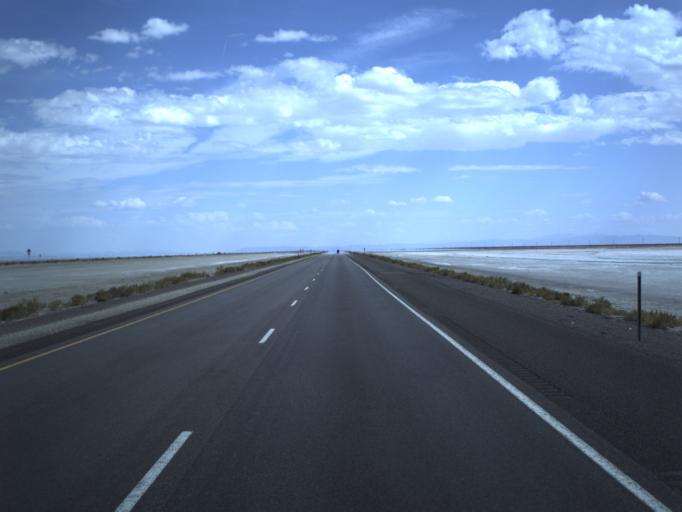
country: US
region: Utah
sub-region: Tooele County
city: Wendover
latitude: 40.7367
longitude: -113.7643
